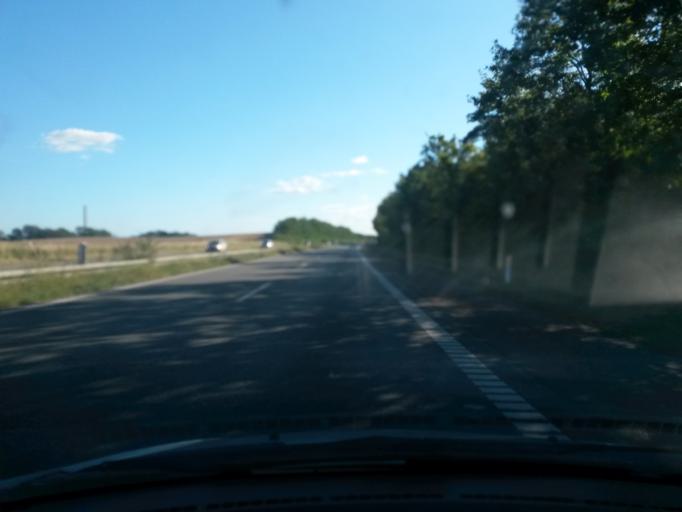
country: DK
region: Central Jutland
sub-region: Arhus Kommune
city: Logten
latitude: 56.2728
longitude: 10.3310
